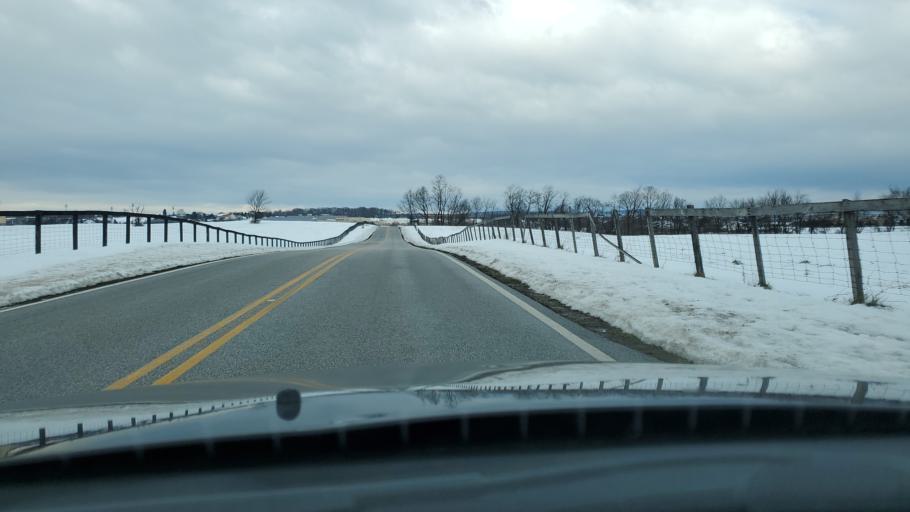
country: US
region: Pennsylvania
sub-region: Cumberland County
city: Mechanicsburg
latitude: 40.2323
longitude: -77.0552
